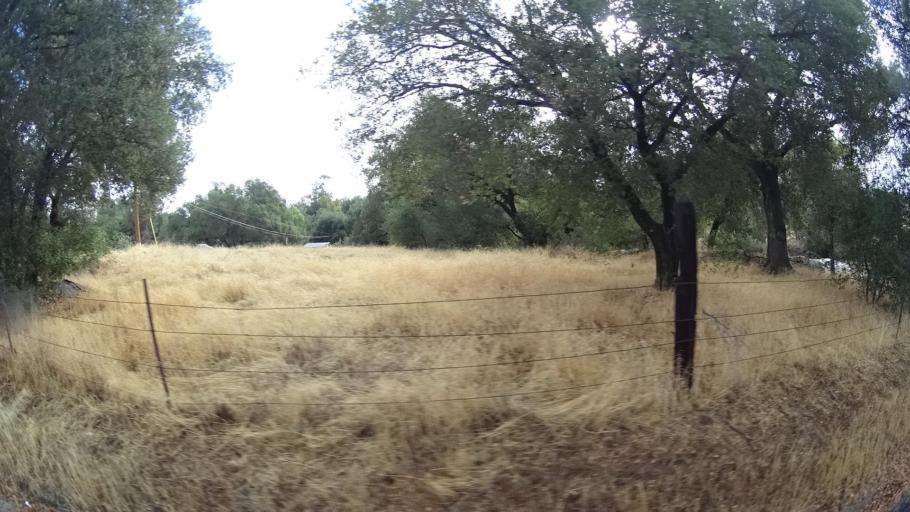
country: MX
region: Baja California
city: Tecate
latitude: 32.6220
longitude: -116.6134
